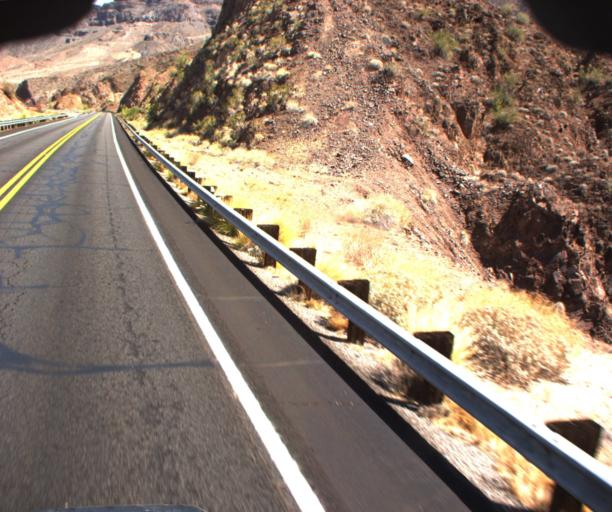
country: US
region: Arizona
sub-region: La Paz County
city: Cienega Springs
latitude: 34.2908
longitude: -114.1152
